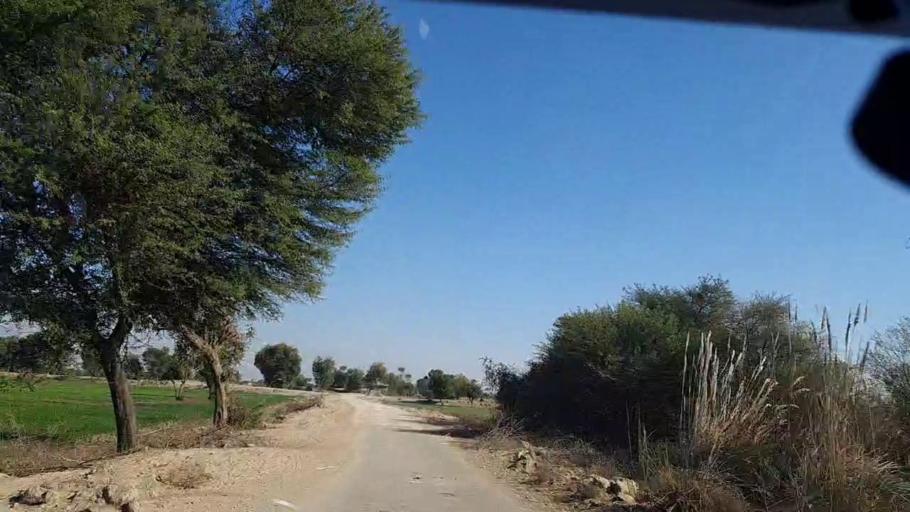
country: PK
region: Sindh
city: Khanpur
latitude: 27.6156
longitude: 69.4480
